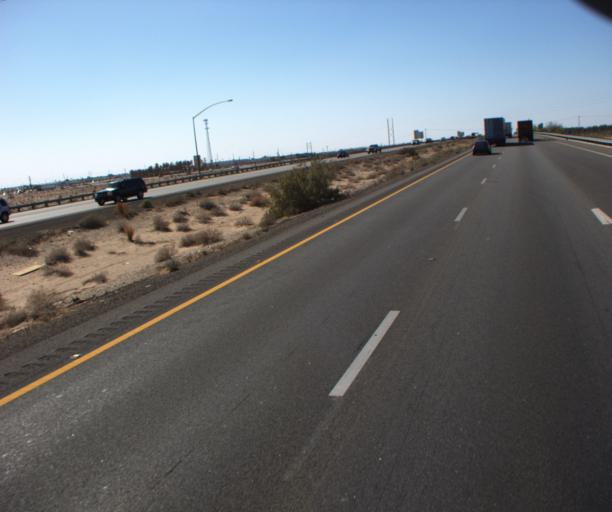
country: US
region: Arizona
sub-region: Yuma County
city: Fortuna Foothills
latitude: 32.6731
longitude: -114.4885
